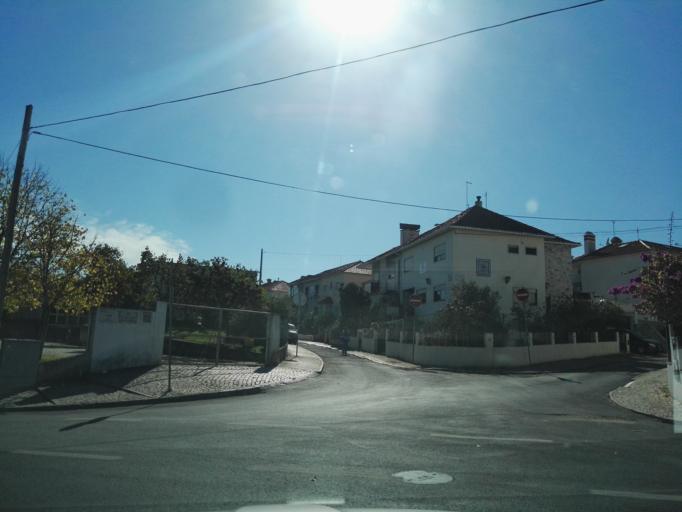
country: PT
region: Lisbon
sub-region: Loures
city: Moscavide
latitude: 38.7739
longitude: -9.1194
